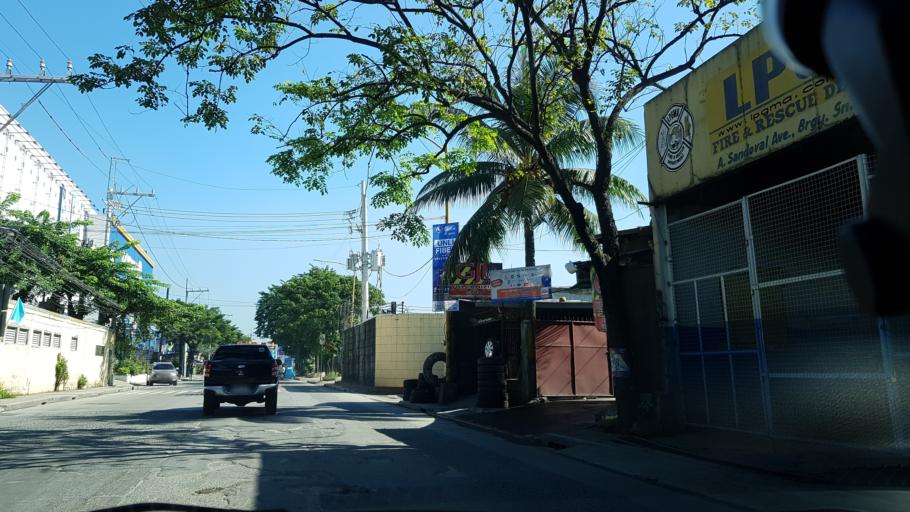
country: PH
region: Calabarzon
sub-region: Province of Rizal
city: Cainta
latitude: 14.5647
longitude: 121.0939
